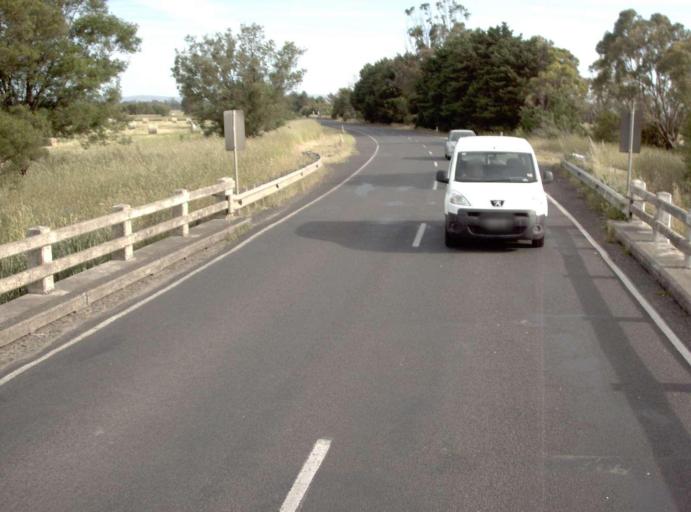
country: AU
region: Victoria
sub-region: Latrobe
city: Traralgon
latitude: -38.1573
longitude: 146.5535
